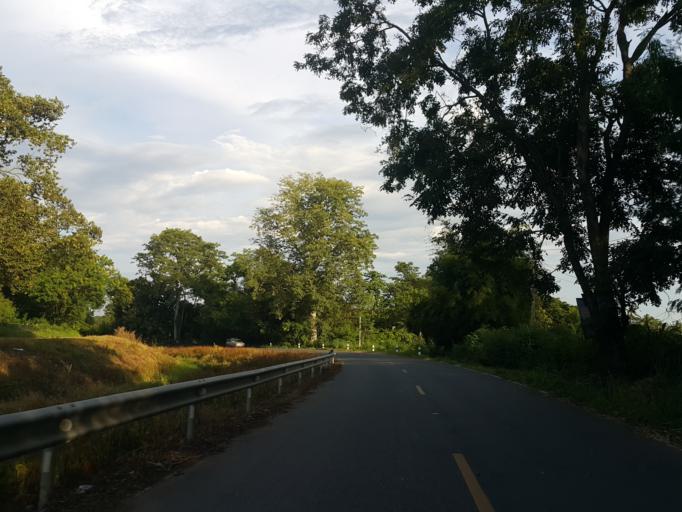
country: TH
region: Chiang Mai
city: San Sai
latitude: 18.9170
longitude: 99.0069
